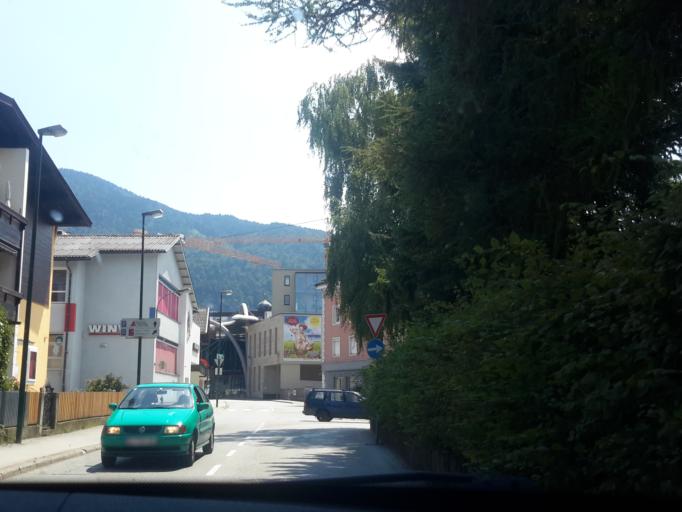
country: AT
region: Tyrol
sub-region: Politischer Bezirk Kufstein
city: Kufstein
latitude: 47.5860
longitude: 12.1698
